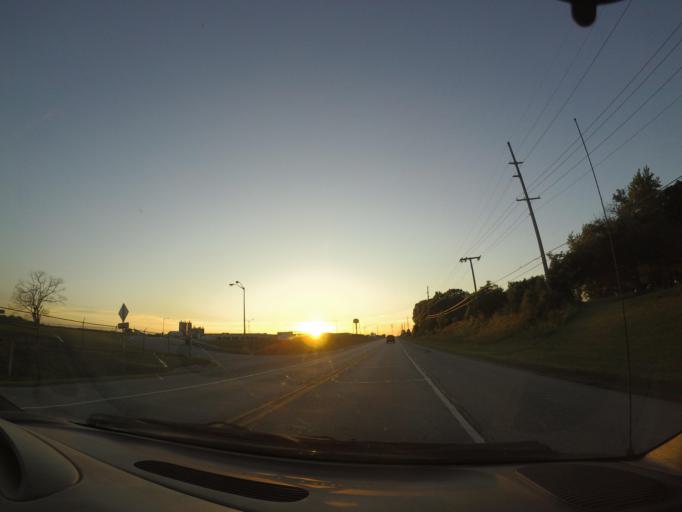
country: US
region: Indiana
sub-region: Elkhart County
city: Middlebury
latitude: 41.6601
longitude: -85.7157
